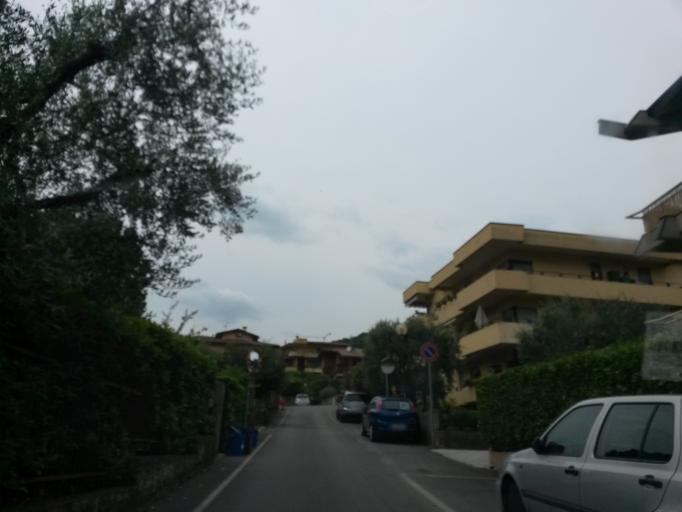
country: IT
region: Lombardy
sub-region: Provincia di Brescia
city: Salo
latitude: 45.6037
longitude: 10.5087
